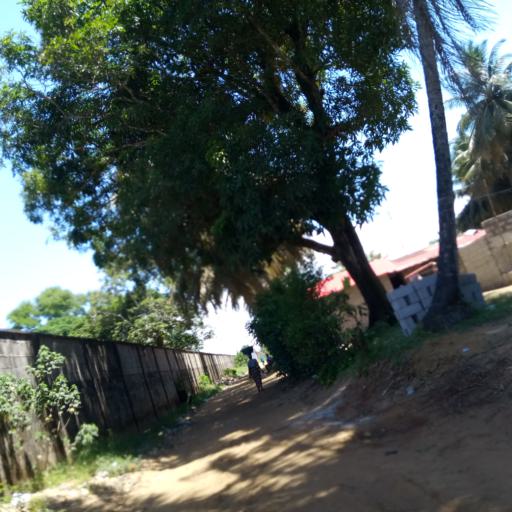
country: LR
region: Montserrado
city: Monrovia
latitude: 6.2372
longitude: -10.6954
